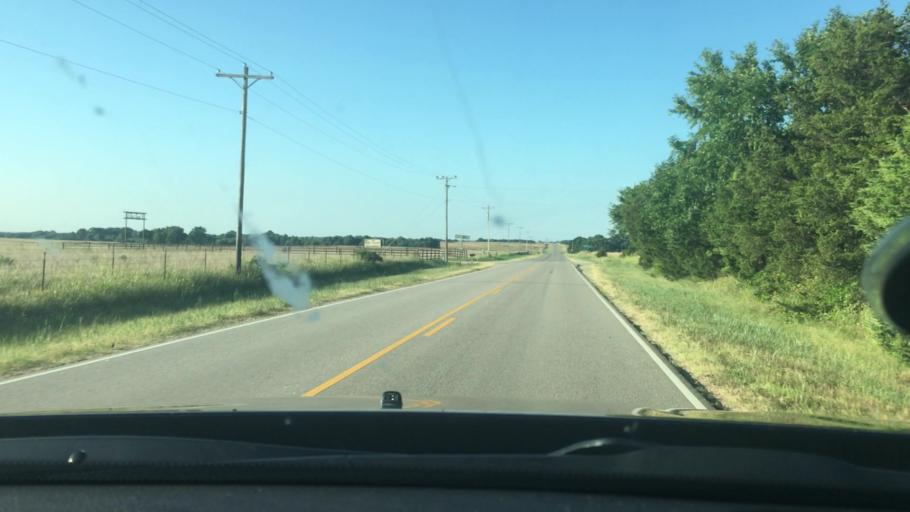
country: US
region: Oklahoma
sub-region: Murray County
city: Sulphur
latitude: 34.5943
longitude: -96.8449
